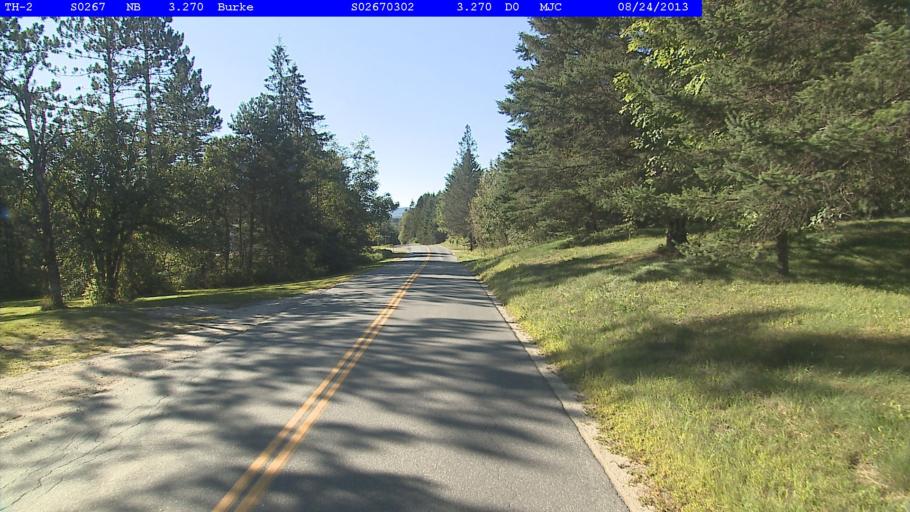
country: US
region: Vermont
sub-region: Caledonia County
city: Lyndonville
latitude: 44.6247
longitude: -71.9585
